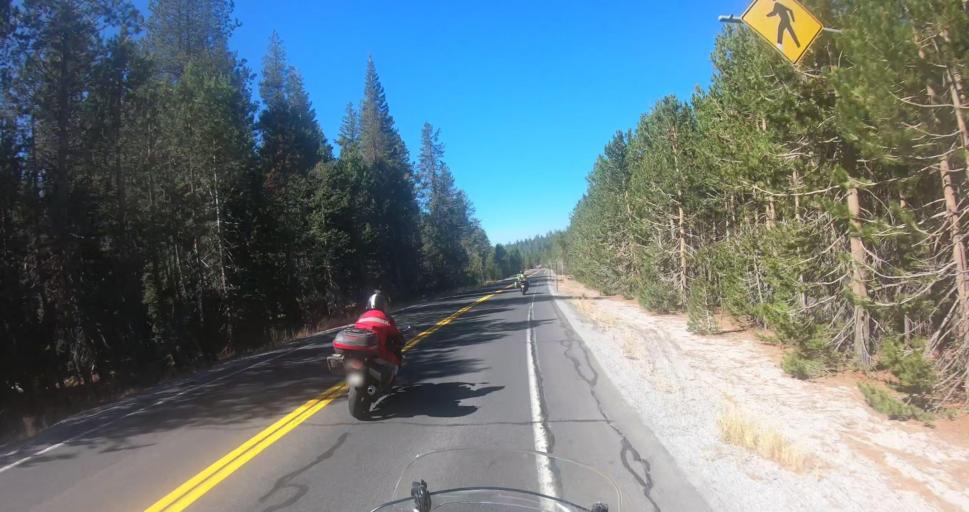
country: US
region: California
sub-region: Calaveras County
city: Arnold
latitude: 38.4614
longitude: -120.0346
